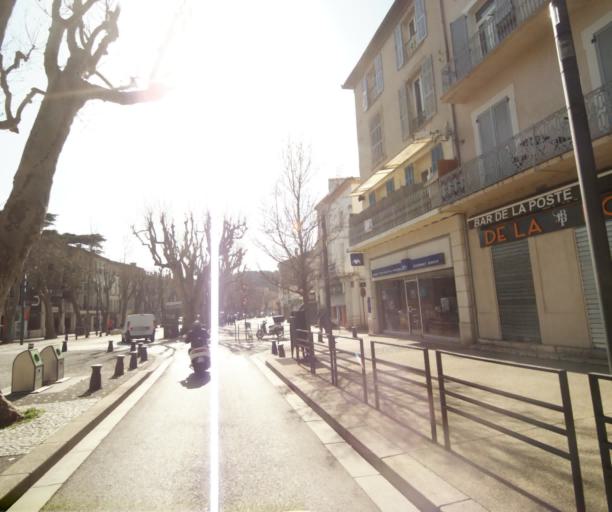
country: FR
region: Provence-Alpes-Cote d'Azur
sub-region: Departement des Bouches-du-Rhone
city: Gardanne
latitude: 43.4553
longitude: 5.4707
